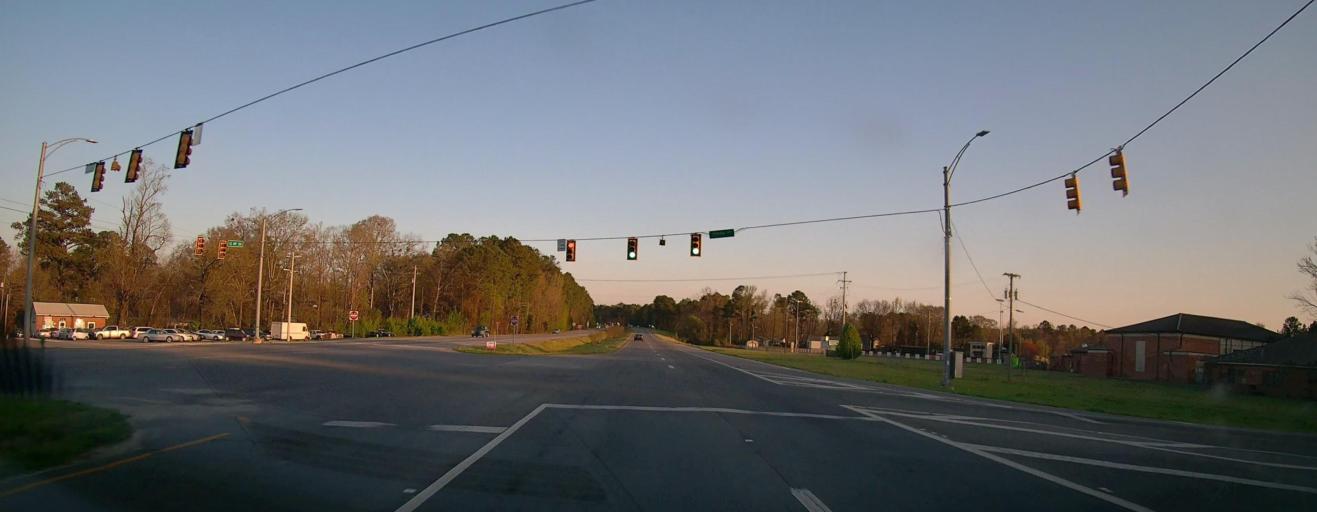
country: US
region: Alabama
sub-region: Talladega County
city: Sylacauga
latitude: 33.1566
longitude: -86.2707
